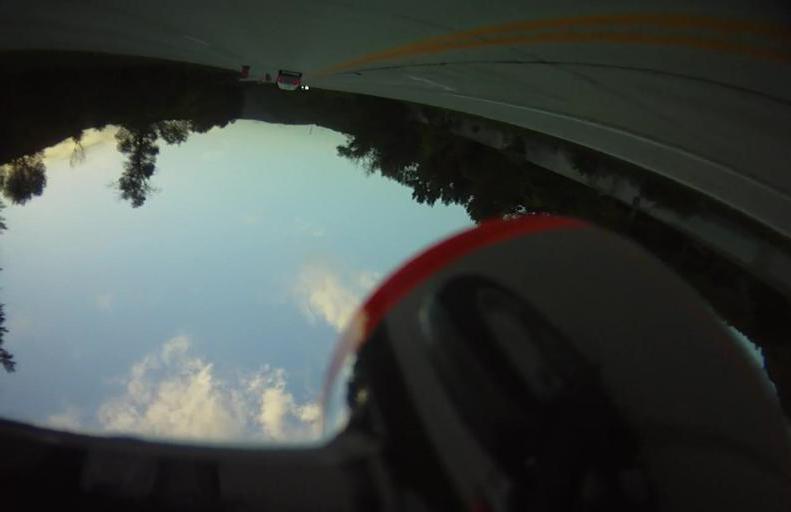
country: US
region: Utah
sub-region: Utah County
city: Orem
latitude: 40.3289
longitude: -111.6215
